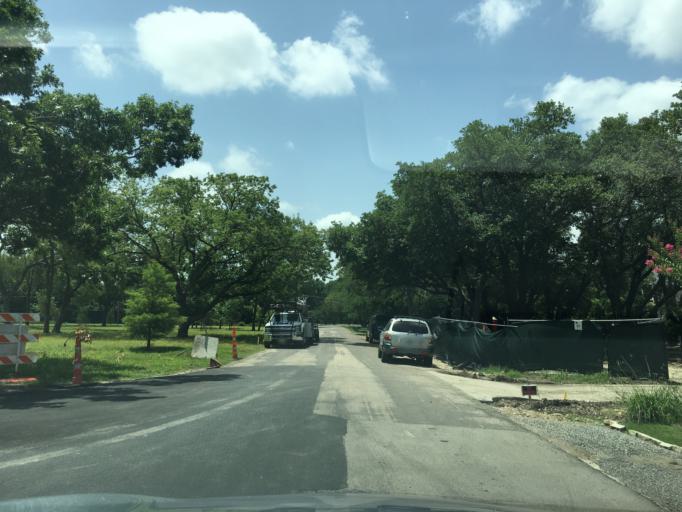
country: US
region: Texas
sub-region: Dallas County
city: University Park
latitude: 32.9036
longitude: -96.7960
